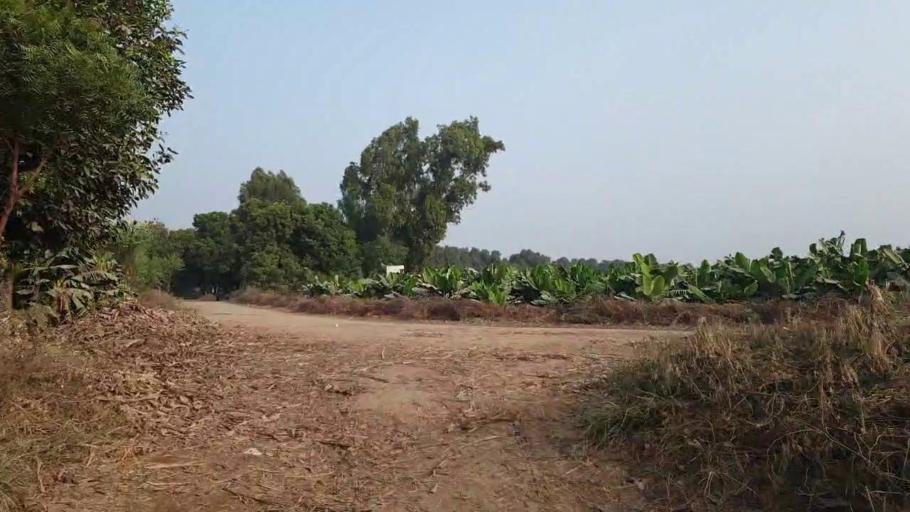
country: PK
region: Sindh
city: Tando Muhammad Khan
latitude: 25.1613
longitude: 68.5840
